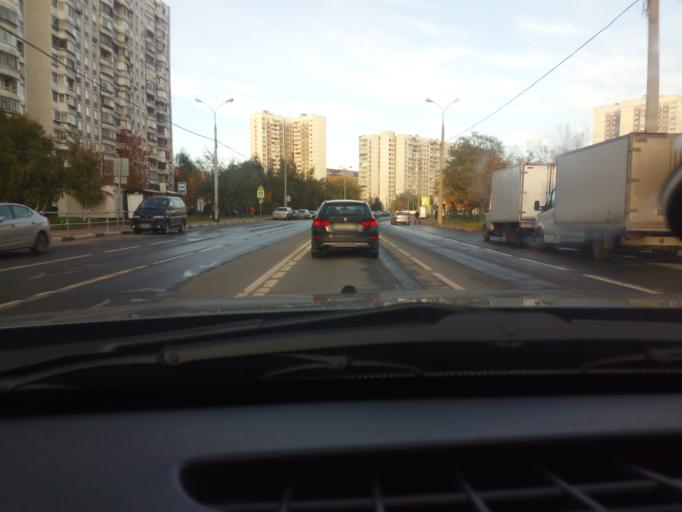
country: RU
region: Moskovskaya
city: Reutov
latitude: 55.7415
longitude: 37.8624
